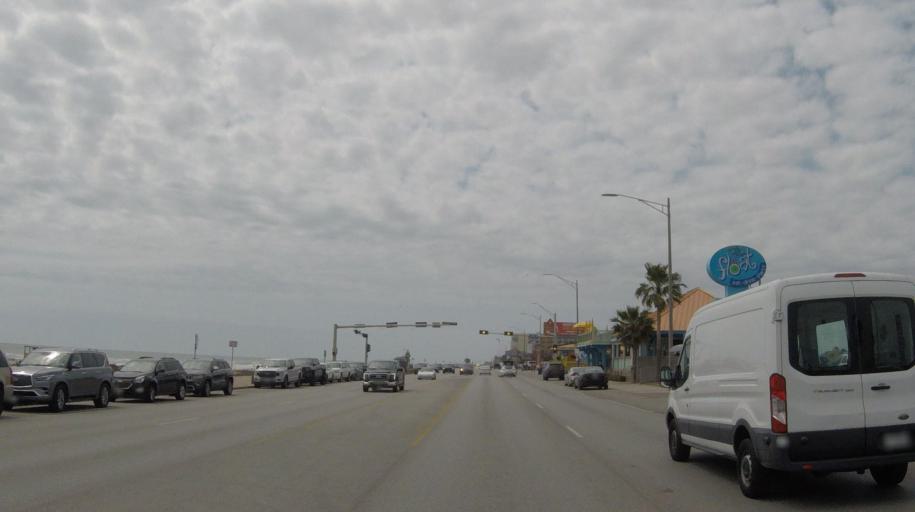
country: US
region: Texas
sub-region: Galveston County
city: Galveston
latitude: 29.2862
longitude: -94.7936
